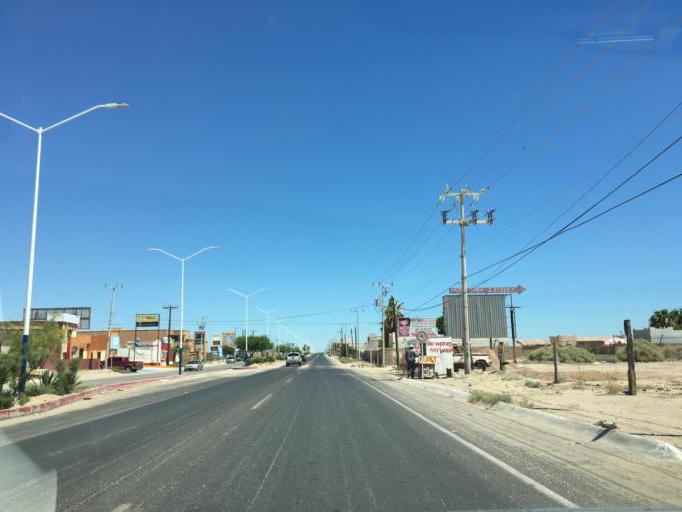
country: MX
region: Sonora
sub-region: Puerto Penasco
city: Puerto Penasco
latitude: 31.3059
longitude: -113.5315
